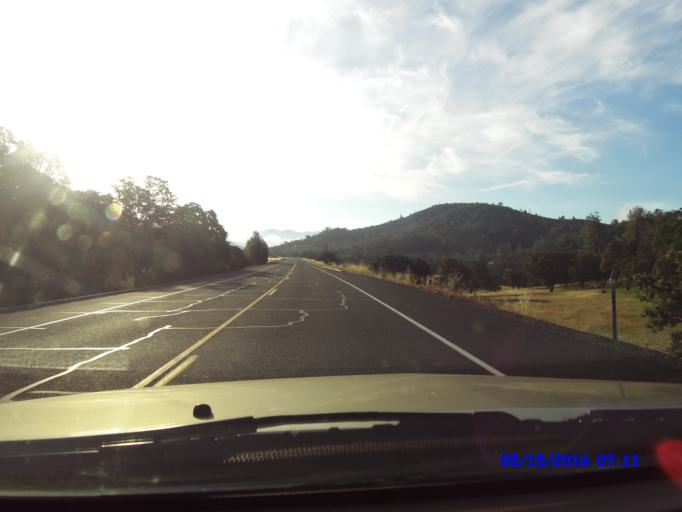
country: US
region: California
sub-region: Tuolumne County
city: Jamestown
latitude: 37.8510
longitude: -120.4092
